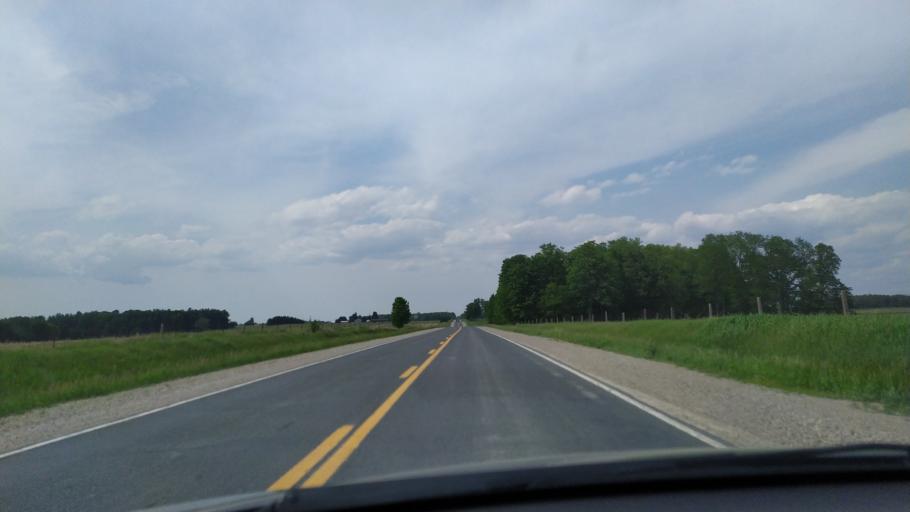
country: CA
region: Ontario
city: Ingersoll
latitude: 43.0262
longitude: -80.9709
